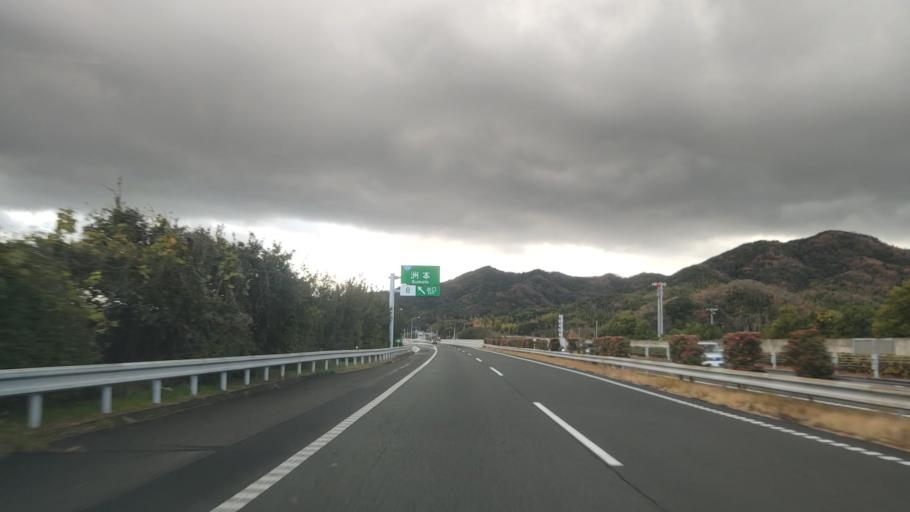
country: JP
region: Hyogo
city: Sumoto
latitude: 34.3436
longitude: 134.8499
